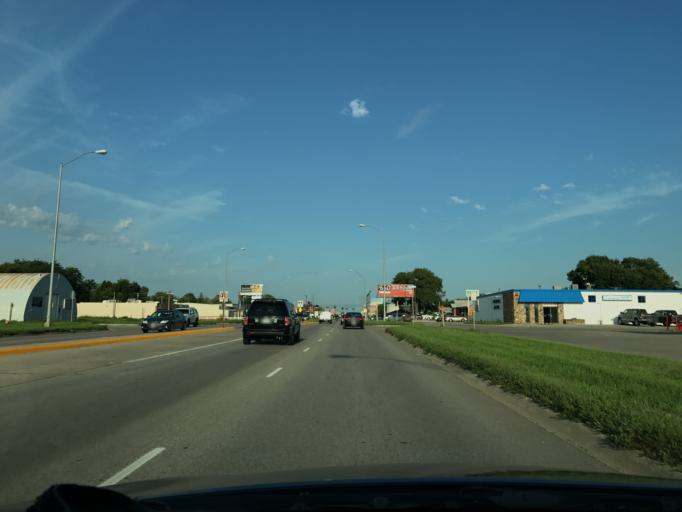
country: US
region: Nebraska
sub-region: Platte County
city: Columbus
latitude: 41.4386
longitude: -97.3452
